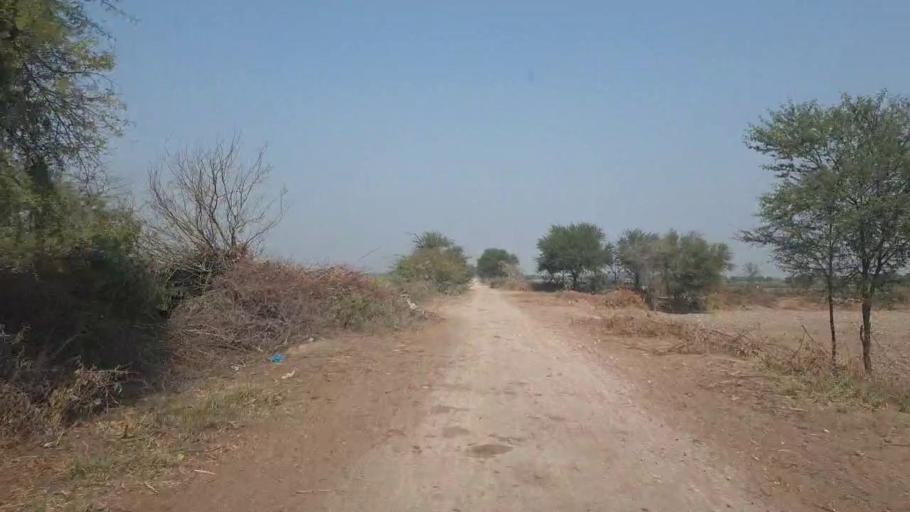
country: PK
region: Sindh
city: Tando Allahyar
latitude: 25.4547
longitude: 68.8319
